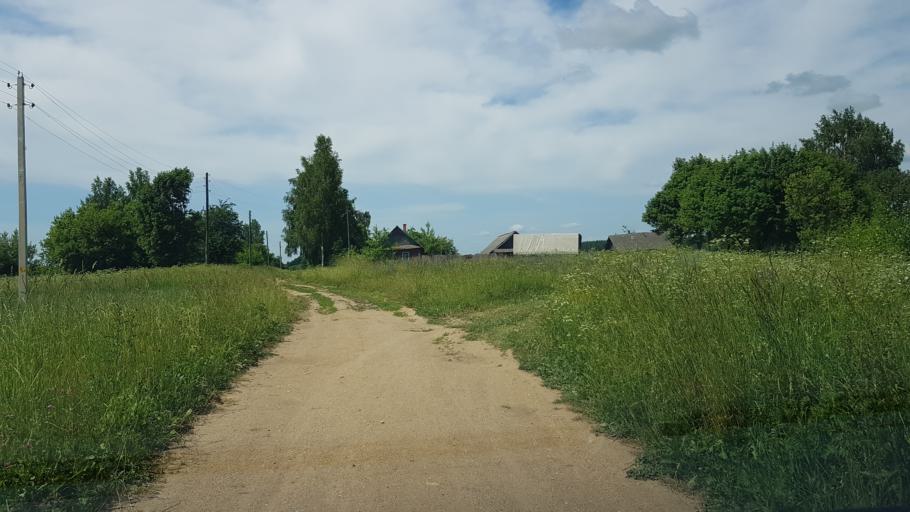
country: BY
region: Vitebsk
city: Dubrowna
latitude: 54.4892
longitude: 30.7936
